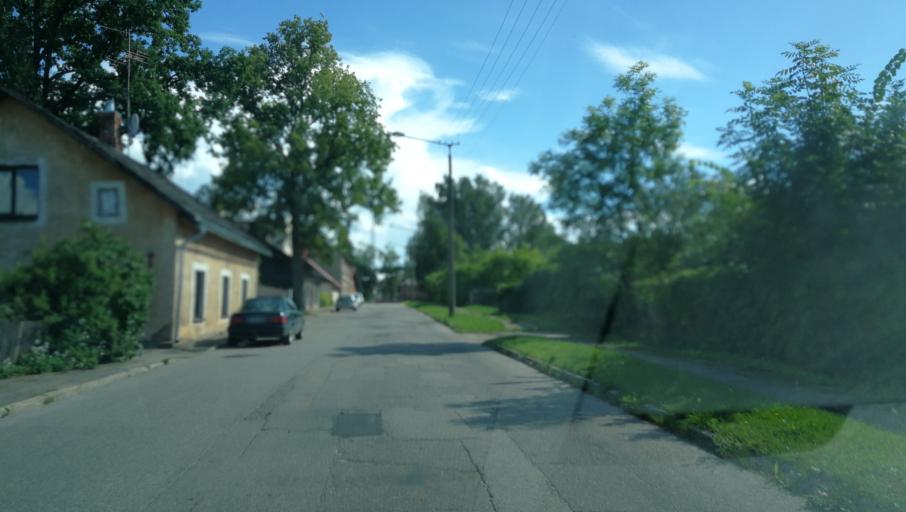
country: LV
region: Cesu Rajons
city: Cesis
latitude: 57.3099
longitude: 25.2571
